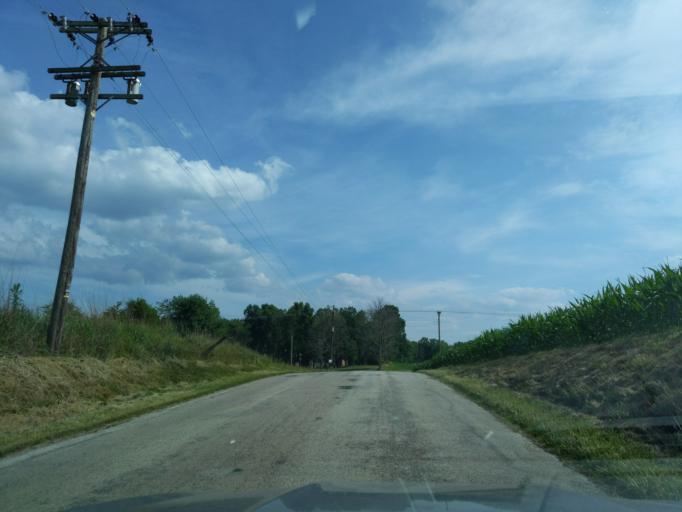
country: US
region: Indiana
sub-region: Decatur County
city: Greensburg
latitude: 39.2936
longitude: -85.4700
